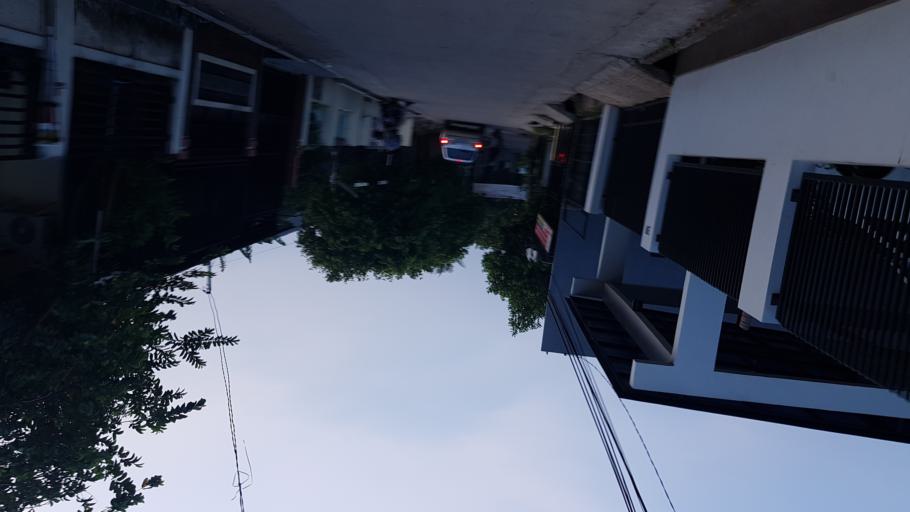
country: ID
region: West Java
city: Bekasi
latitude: -6.2665
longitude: 106.9291
